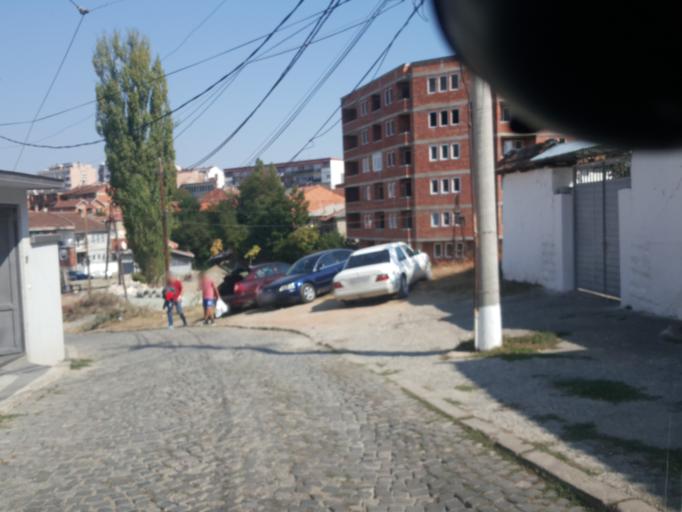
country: XK
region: Gjakova
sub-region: Komuna e Gjakoves
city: Gjakove
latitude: 42.3836
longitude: 20.4263
